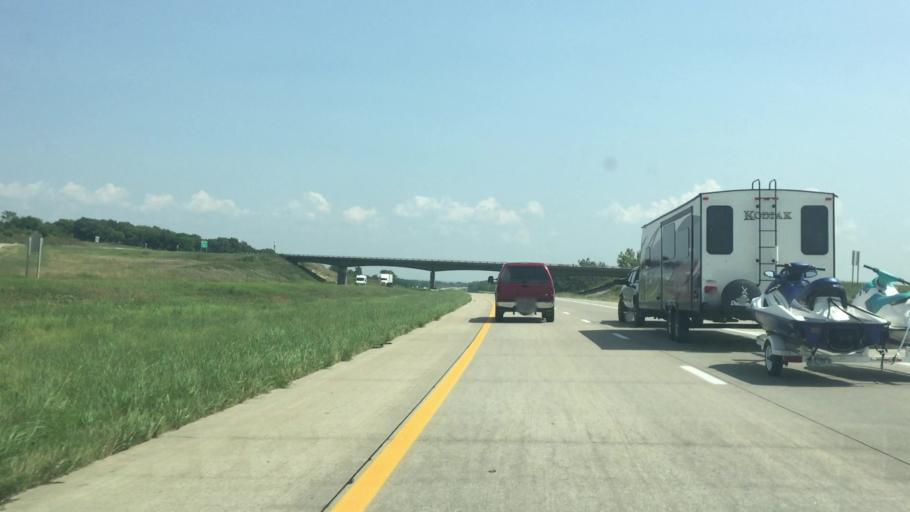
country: US
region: Kansas
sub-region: Franklin County
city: Ottawa
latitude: 38.5338
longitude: -95.3805
